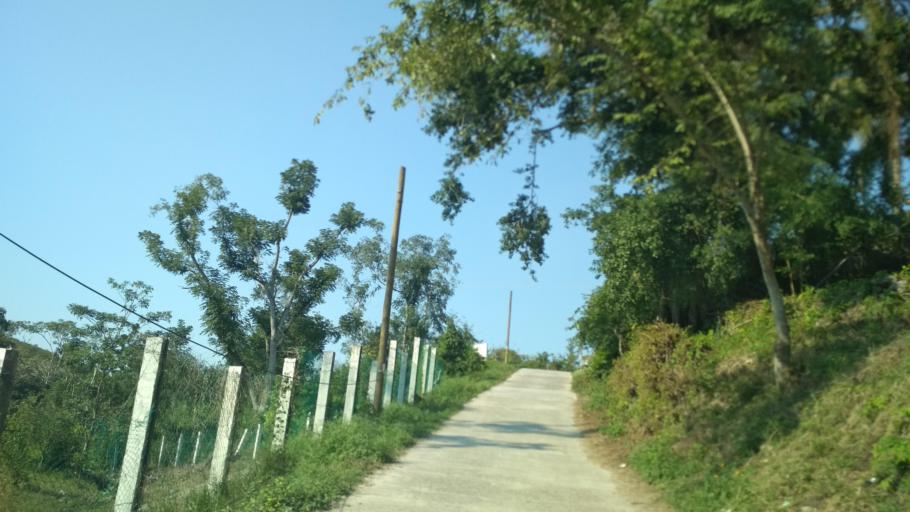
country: MX
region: Veracruz
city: Agua Dulce
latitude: 20.3934
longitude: -97.2107
